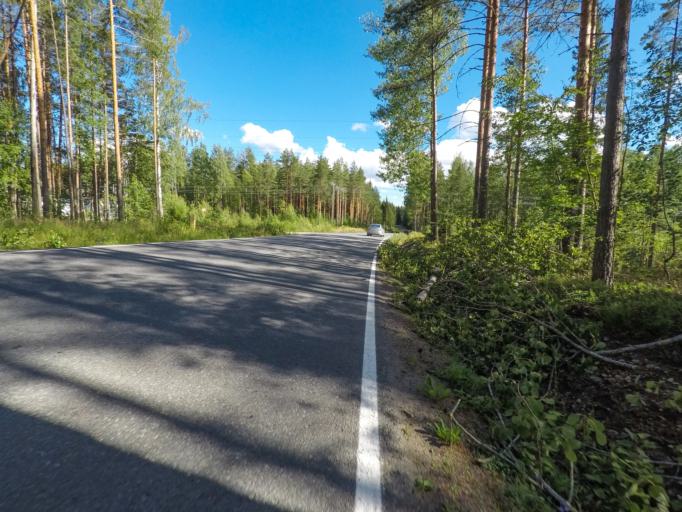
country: FI
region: South Karelia
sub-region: Lappeenranta
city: Taipalsaari
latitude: 61.1761
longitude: 28.0132
